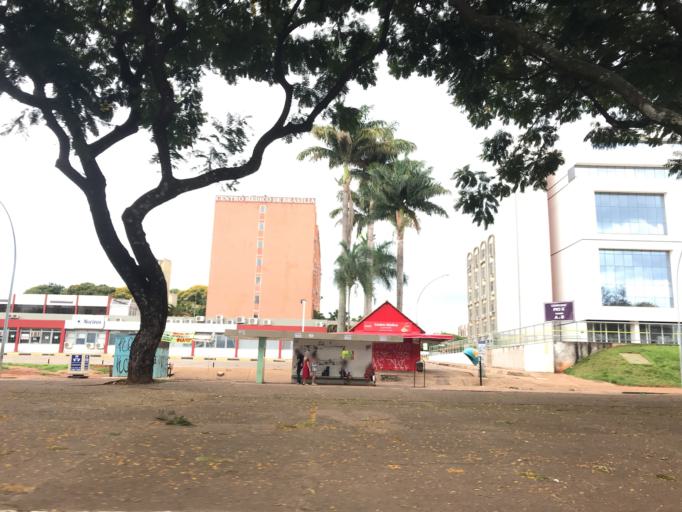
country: BR
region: Federal District
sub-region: Brasilia
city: Brasilia
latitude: -15.8283
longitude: -47.9279
